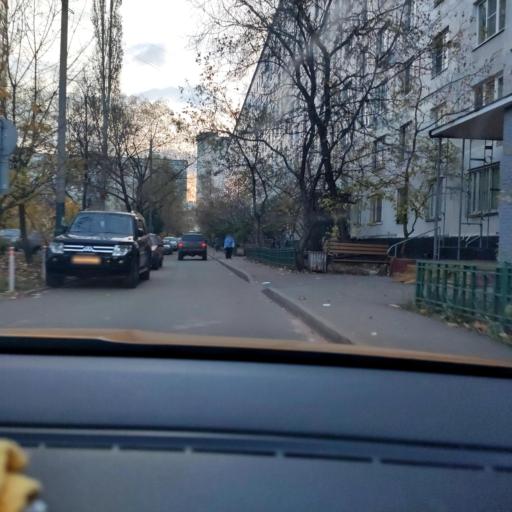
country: RU
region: Moscow
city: Gol'yanovo
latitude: 55.8210
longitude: 37.8197
